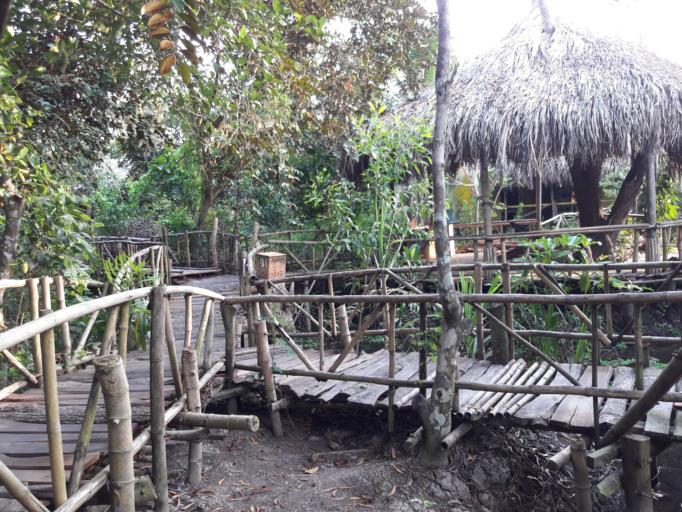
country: VN
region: Can Tho
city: Cai Rang
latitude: 10.0204
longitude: 105.7399
